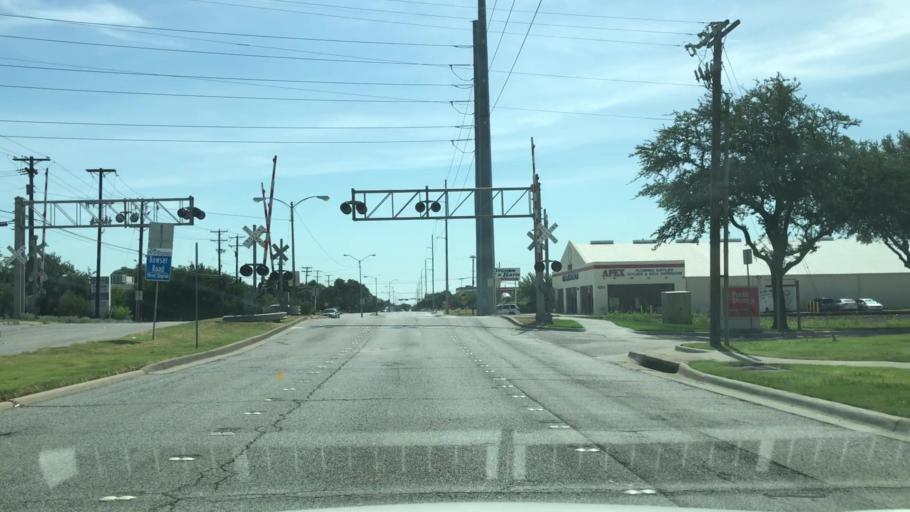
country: US
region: Texas
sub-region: Dallas County
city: Richardson
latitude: 32.9607
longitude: -96.7176
